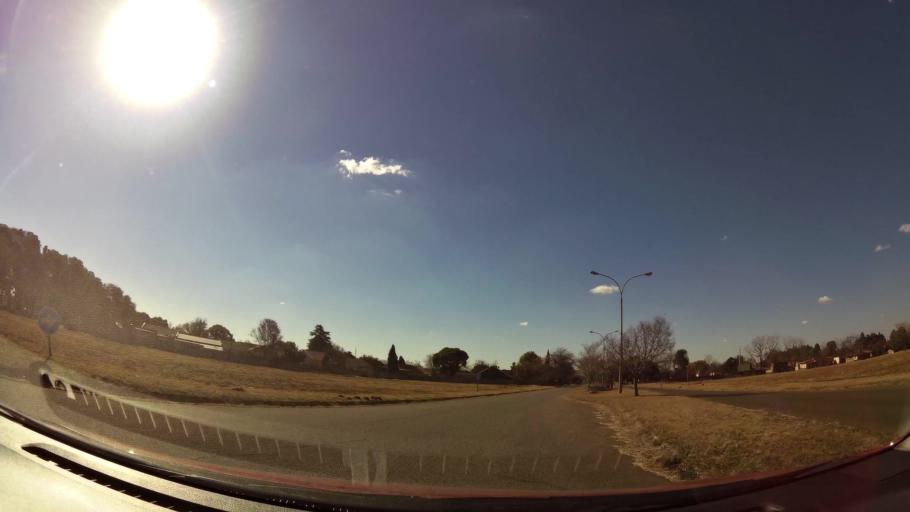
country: ZA
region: Gauteng
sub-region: West Rand District Municipality
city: Carletonville
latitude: -26.3672
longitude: 27.3775
